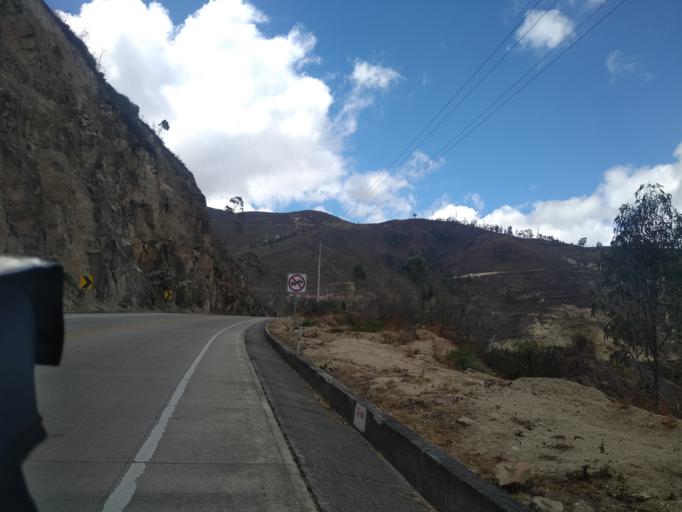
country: EC
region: El Oro
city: Zaruma
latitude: -3.4407
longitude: -79.1590
